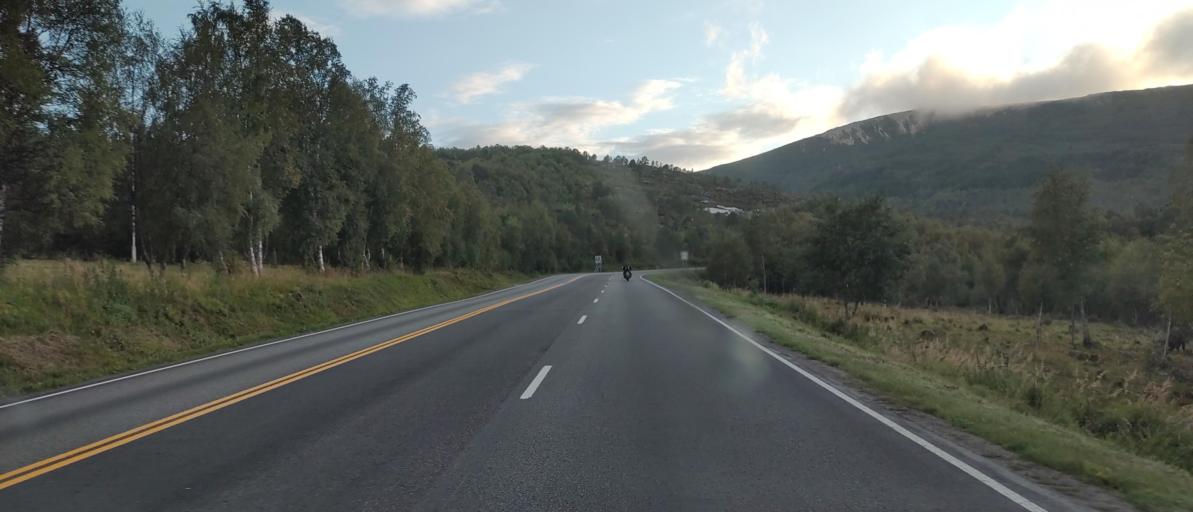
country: NO
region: Nordland
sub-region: Lodingen
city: Lodingen
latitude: 68.2184
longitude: 16.0667
